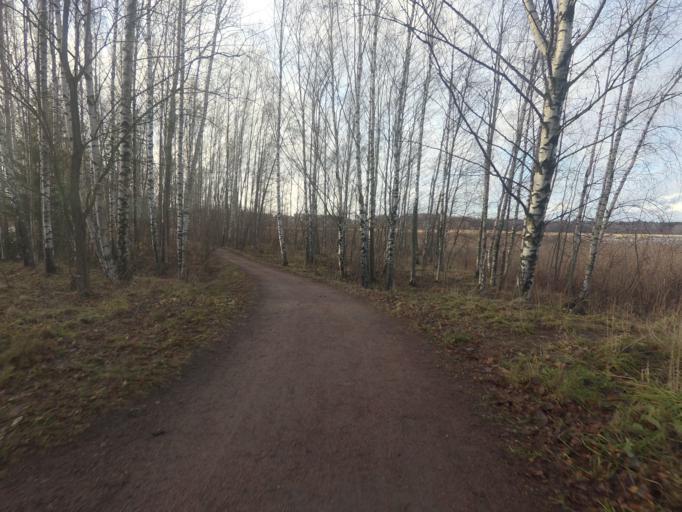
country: FI
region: Uusimaa
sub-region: Helsinki
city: Otaniemi
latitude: 60.1897
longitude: 24.8250
